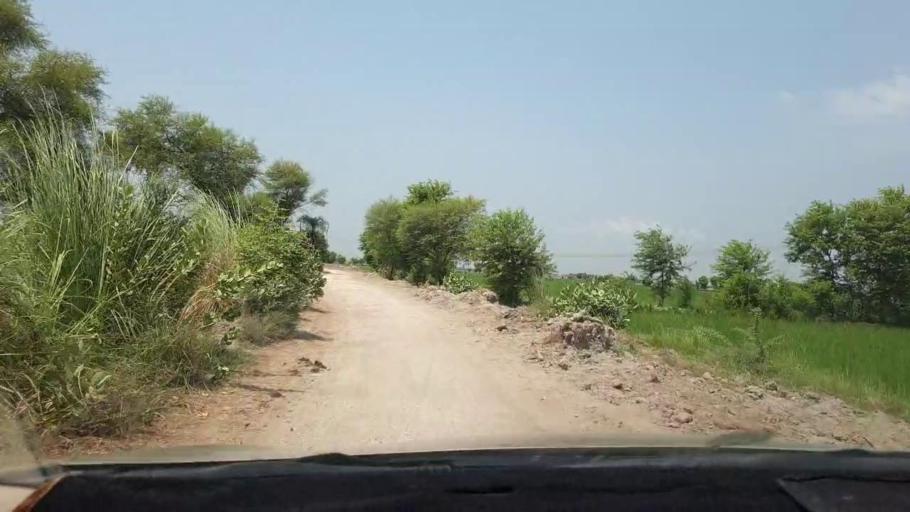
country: PK
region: Sindh
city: Naudero
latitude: 27.6648
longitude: 68.3105
